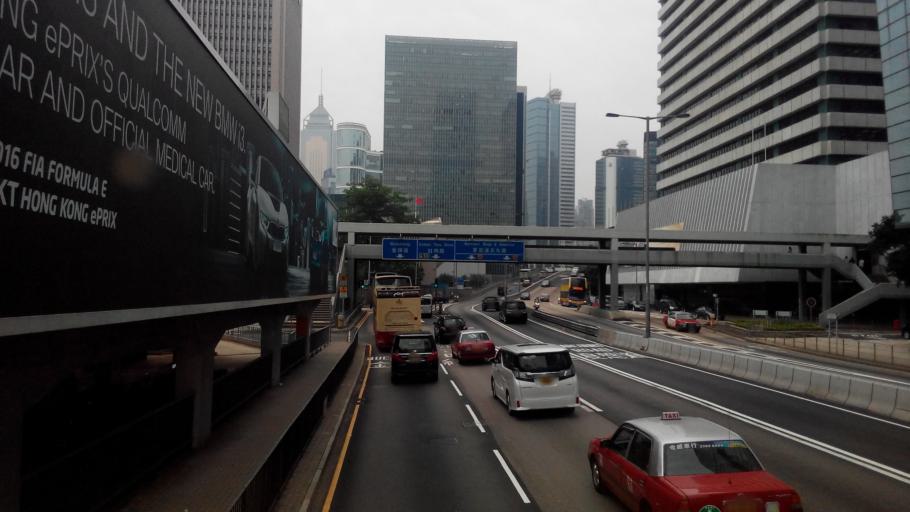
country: HK
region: Central and Western
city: Central
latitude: 22.2814
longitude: 114.1617
